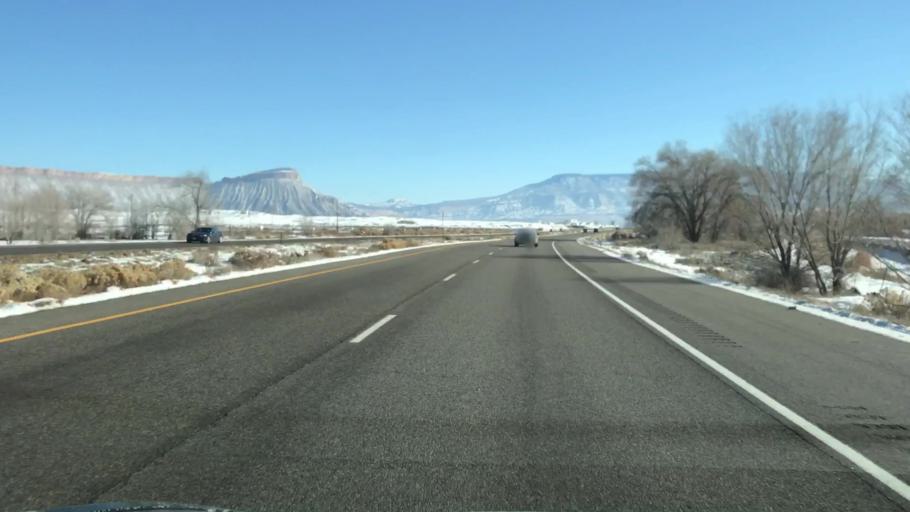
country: US
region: Colorado
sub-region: Mesa County
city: Fruitvale
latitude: 39.1086
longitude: -108.5051
